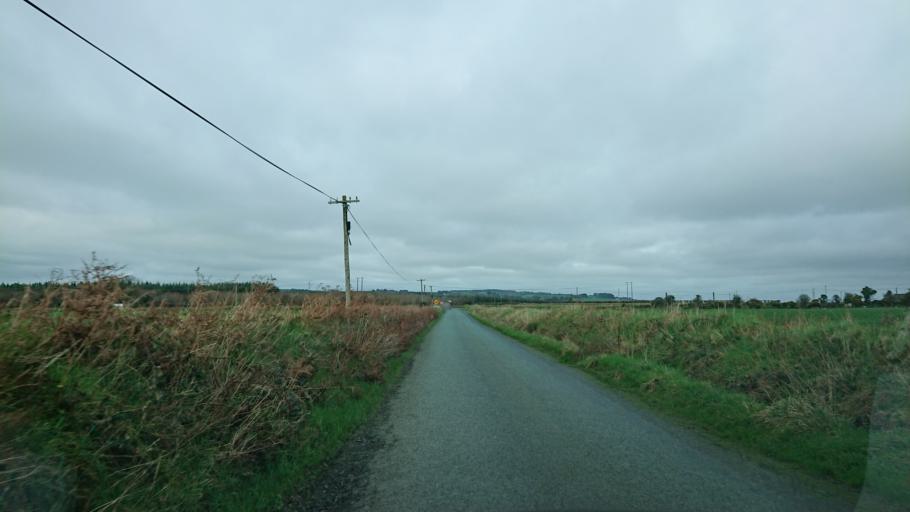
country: IE
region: Munster
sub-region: Waterford
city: Portlaw
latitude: 52.1799
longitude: -7.3028
